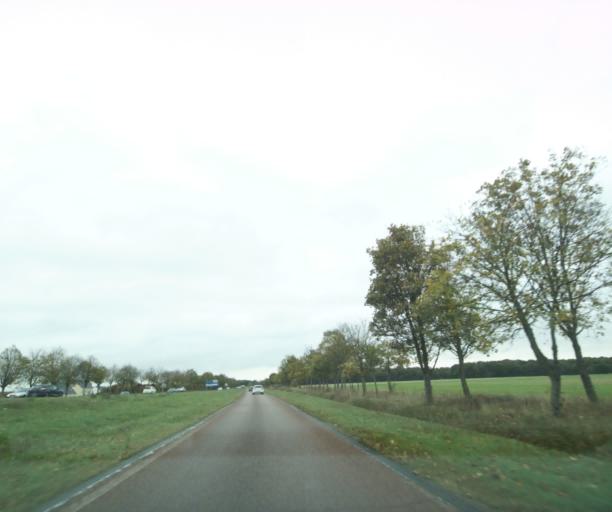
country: FR
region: Centre
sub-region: Departement d'Eure-et-Loir
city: Vernouillet
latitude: 48.7184
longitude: 1.3805
